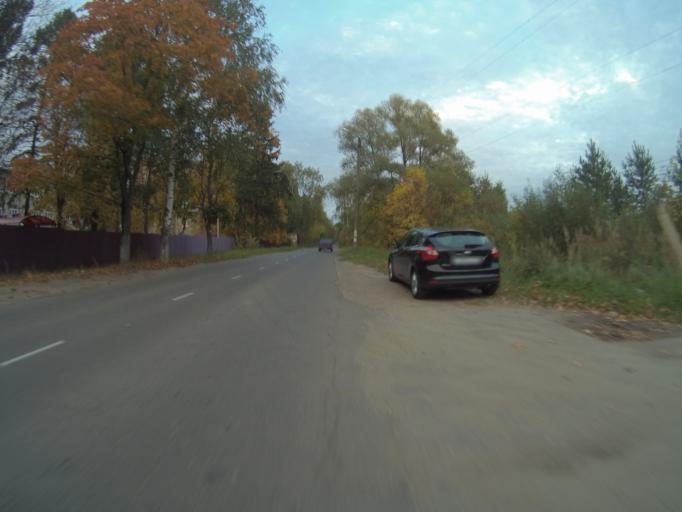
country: RU
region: Vladimir
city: Sobinka
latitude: 56.0008
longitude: 40.0546
